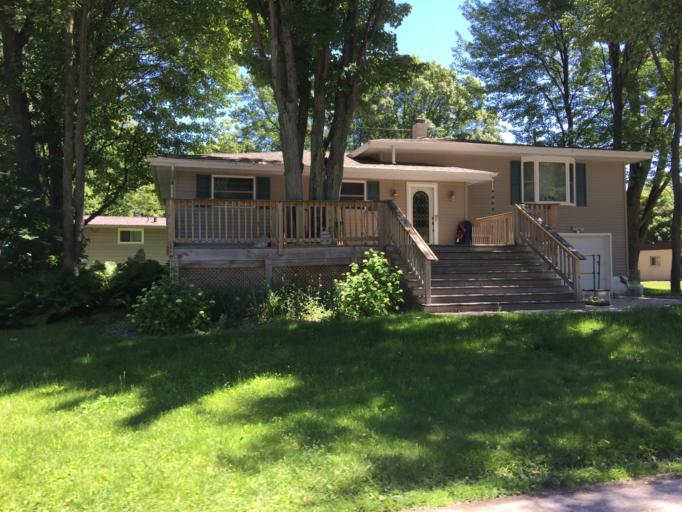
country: US
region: Michigan
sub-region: Menominee County
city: Menominee
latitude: 45.1289
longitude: -87.6235
